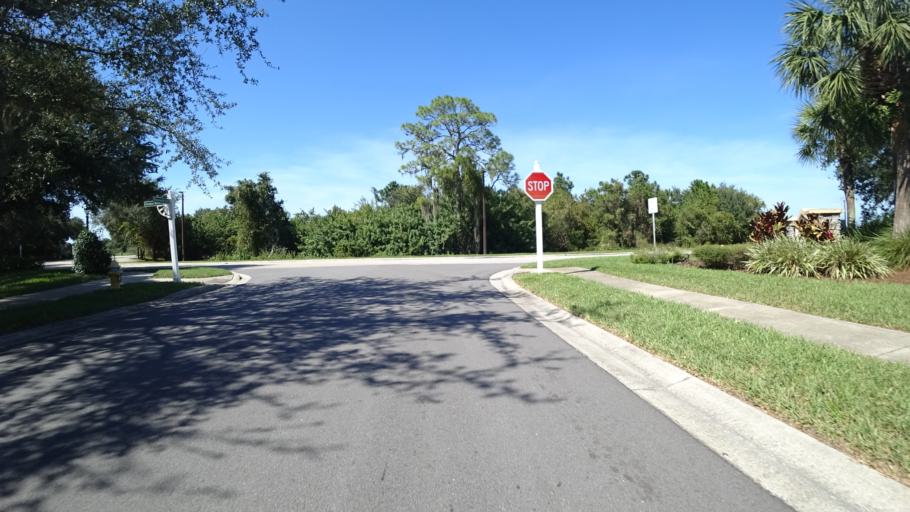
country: US
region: Florida
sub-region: Sarasota County
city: The Meadows
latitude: 27.4149
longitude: -82.4247
